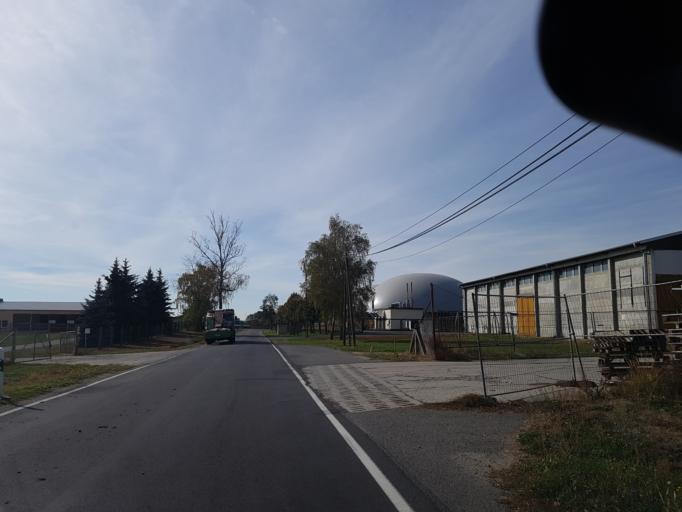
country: DE
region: Brandenburg
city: Schlieben
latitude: 51.7158
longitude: 13.4121
